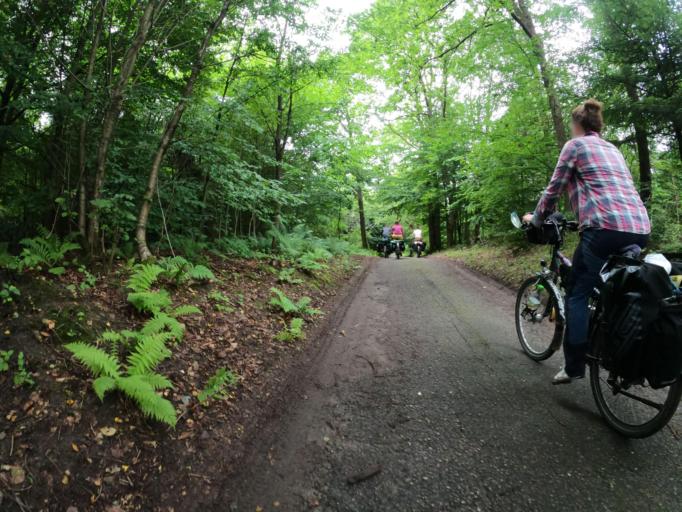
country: PL
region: West Pomeranian Voivodeship
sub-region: Powiat szczecinecki
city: Grzmiaca
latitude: 53.9631
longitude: 16.4498
